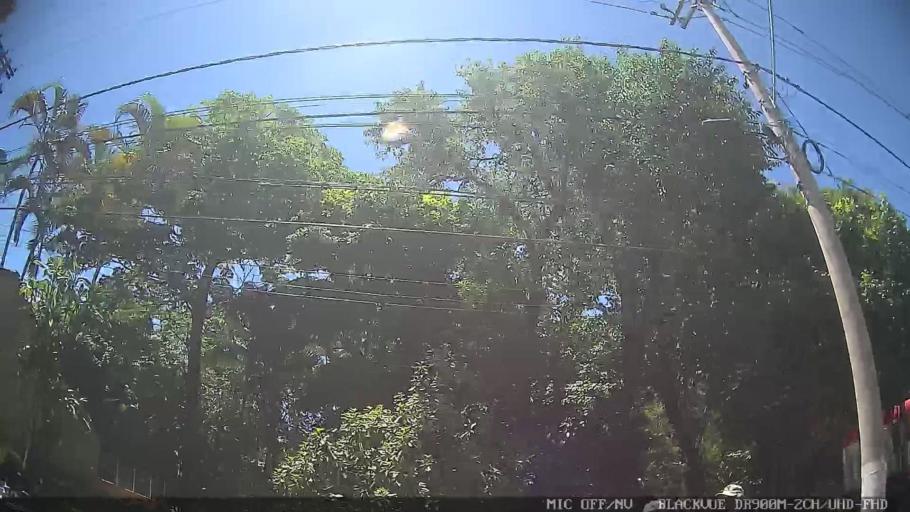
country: BR
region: Sao Paulo
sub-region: Pedreira
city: Pedreira
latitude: -22.7424
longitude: -46.9098
